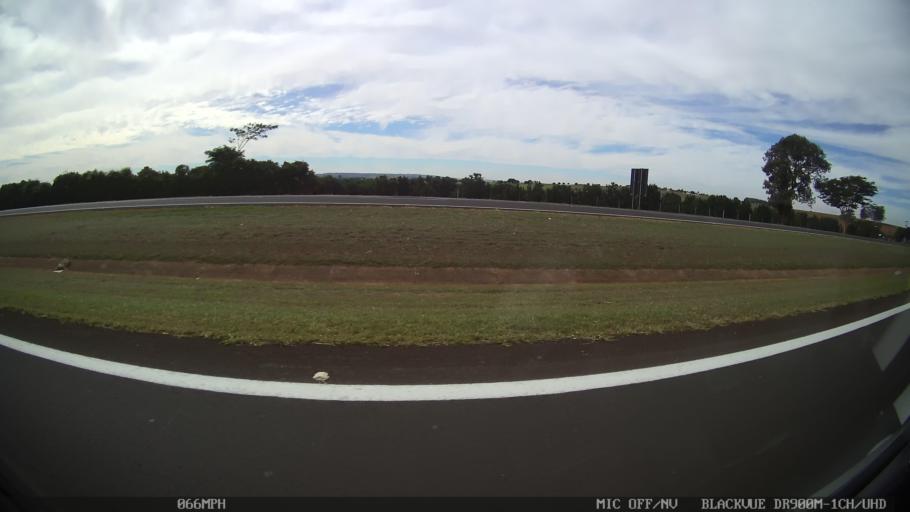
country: BR
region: Sao Paulo
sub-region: Taquaritinga
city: Taquaritinga
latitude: -21.4639
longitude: -48.6153
